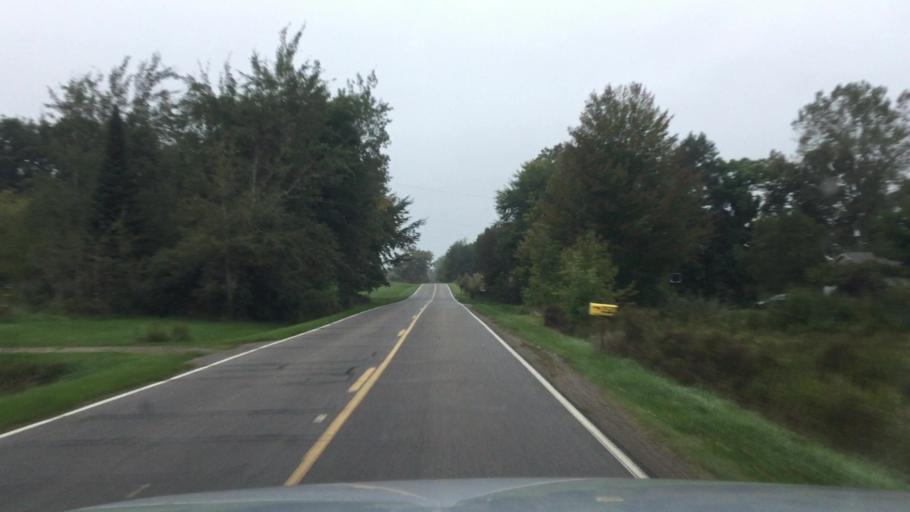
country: US
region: Michigan
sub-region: Shiawassee County
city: Corunna
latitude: 42.9379
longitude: -84.1330
